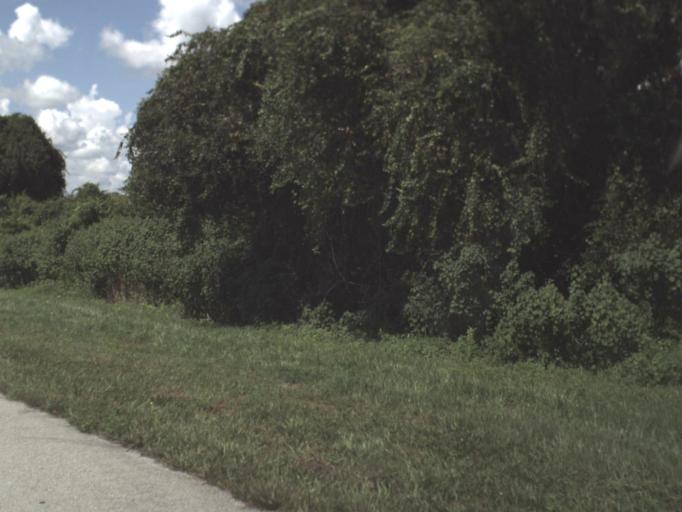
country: US
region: Florida
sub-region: DeSoto County
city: Nocatee
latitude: 27.1162
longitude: -81.9207
